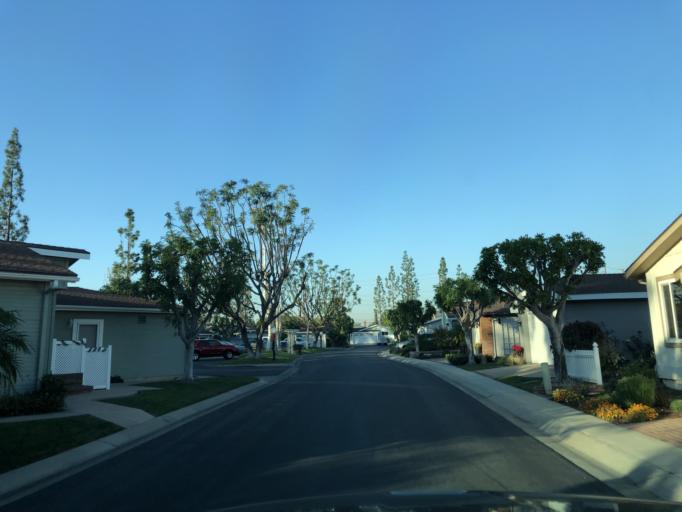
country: US
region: California
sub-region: Orange County
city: Orange
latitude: 33.7718
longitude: -117.8455
